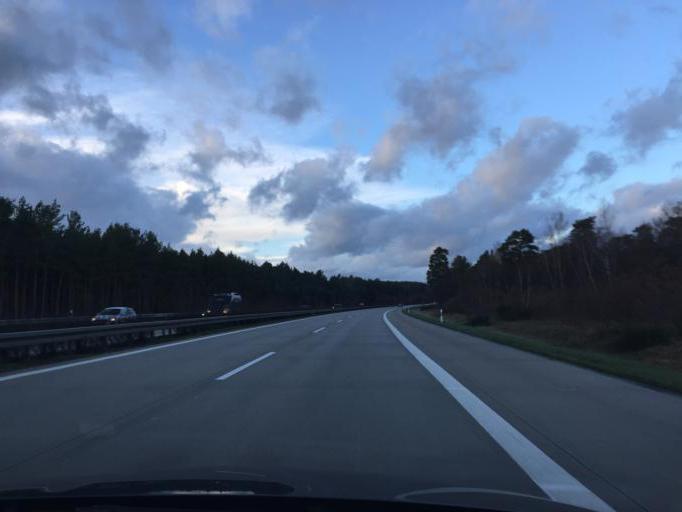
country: DE
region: Brandenburg
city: Schwerin
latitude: 52.1750
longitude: 13.6265
